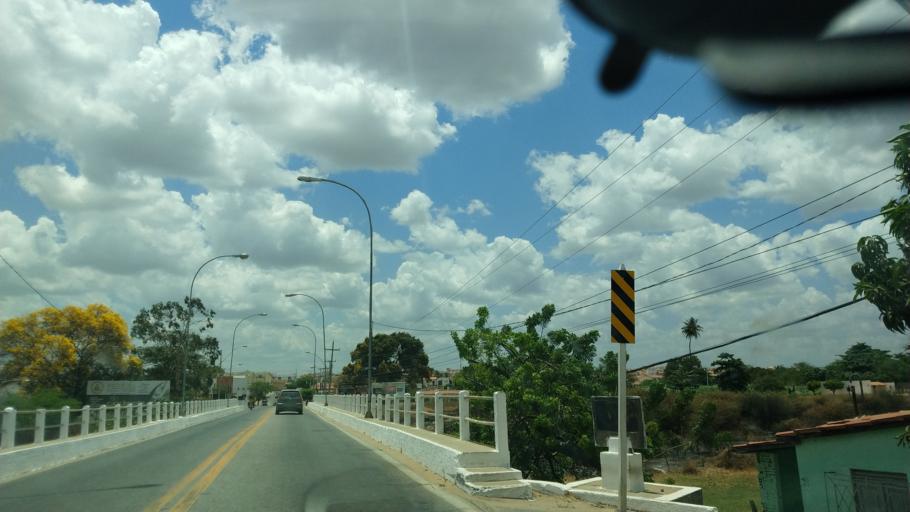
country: BR
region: Rio Grande do Norte
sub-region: Currais Novos
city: Currais Novos
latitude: -6.2577
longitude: -36.5102
